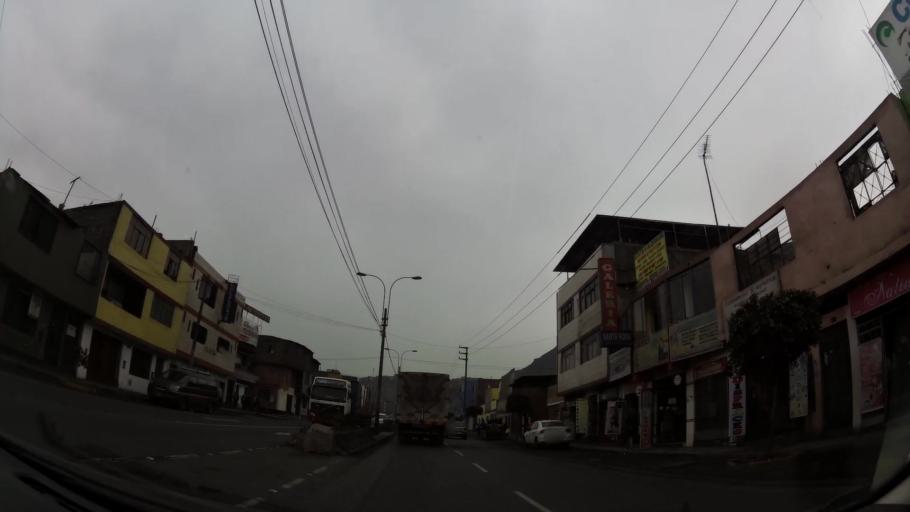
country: PE
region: Lima
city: Lima
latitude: -12.0462
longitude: -76.9992
